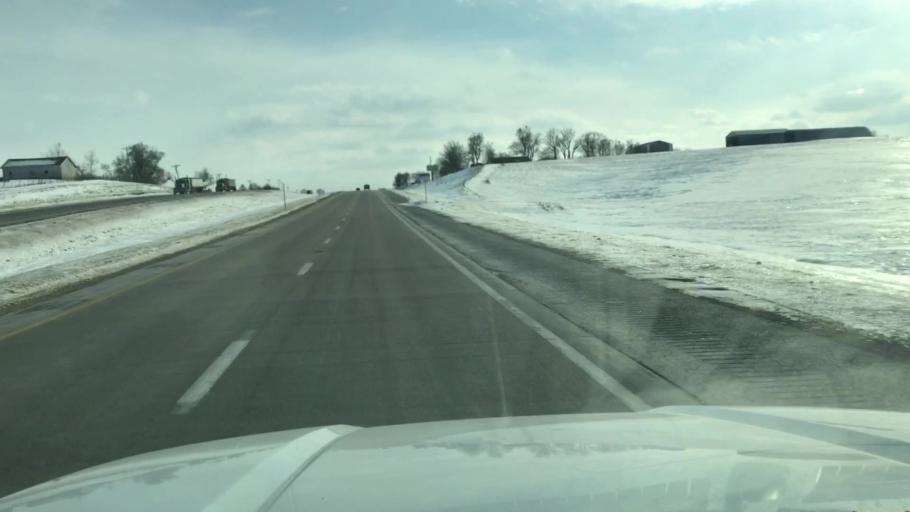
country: US
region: Missouri
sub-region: Nodaway County
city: Maryville
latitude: 40.2949
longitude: -94.8754
